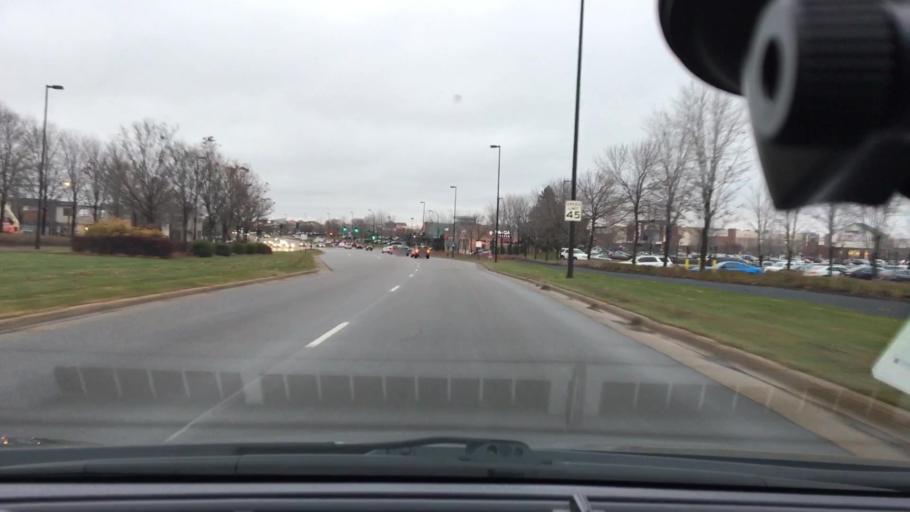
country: US
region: Minnesota
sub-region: Hennepin County
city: Maple Grove
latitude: 45.0953
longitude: -93.4448
